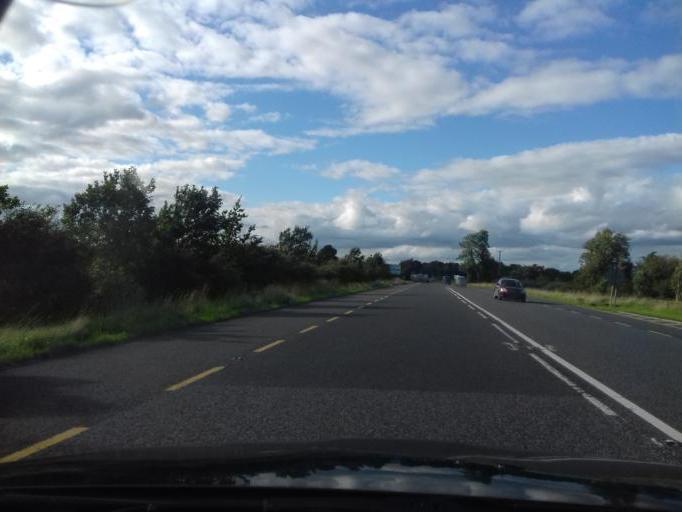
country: IE
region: Leinster
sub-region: Uibh Fhaili
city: Tullamore
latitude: 53.3073
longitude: -7.4955
